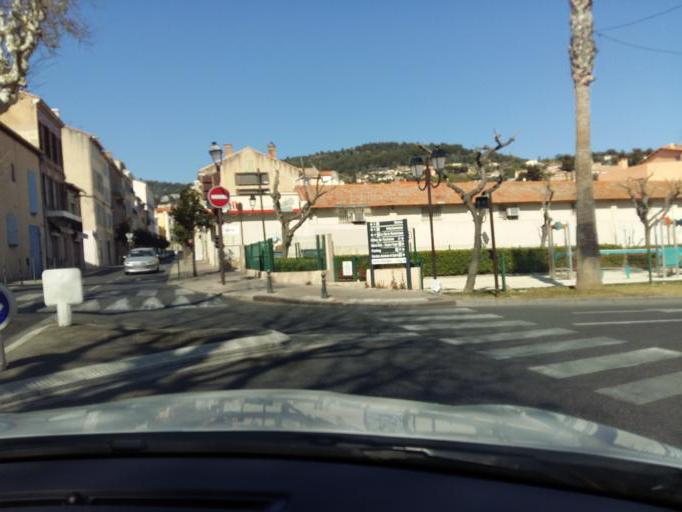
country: FR
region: Provence-Alpes-Cote d'Azur
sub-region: Departement du Var
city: Ollioules
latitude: 43.1380
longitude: 5.8474
